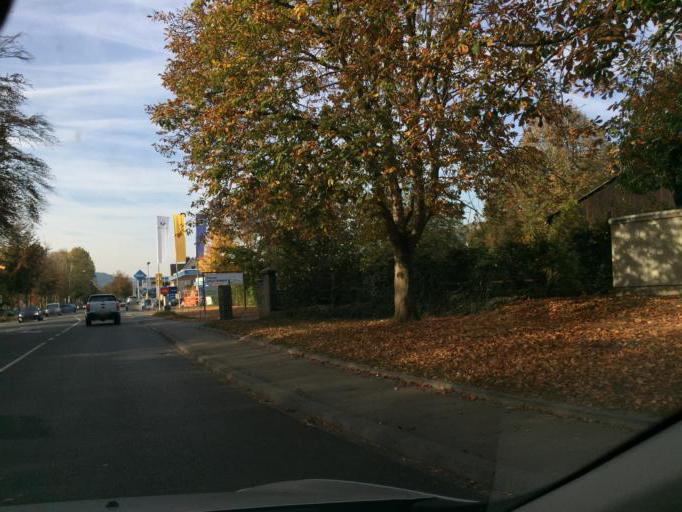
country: LU
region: Diekirch
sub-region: Canton de Diekirch
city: Diekirch
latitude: 49.8628
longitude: 6.1504
